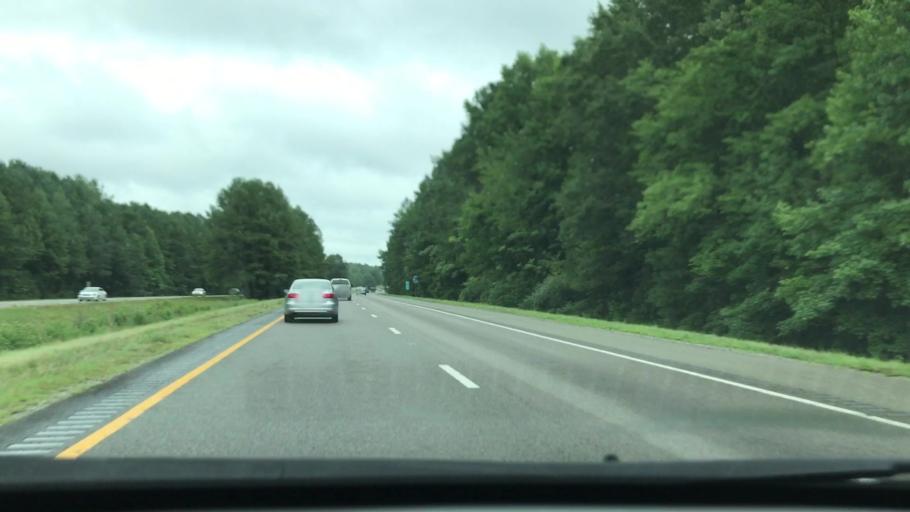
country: US
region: Virginia
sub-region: Sussex County
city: Sussex
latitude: 37.0416
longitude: -77.3871
